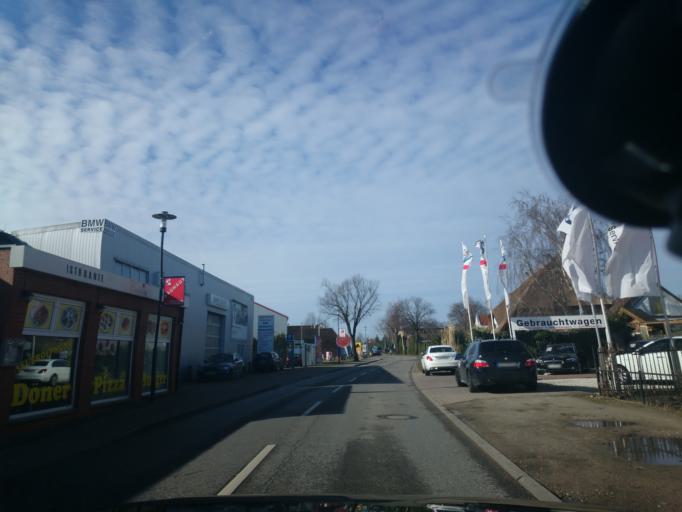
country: DE
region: Mecklenburg-Vorpommern
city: Elmenhorst
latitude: 54.1554
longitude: 12.0155
